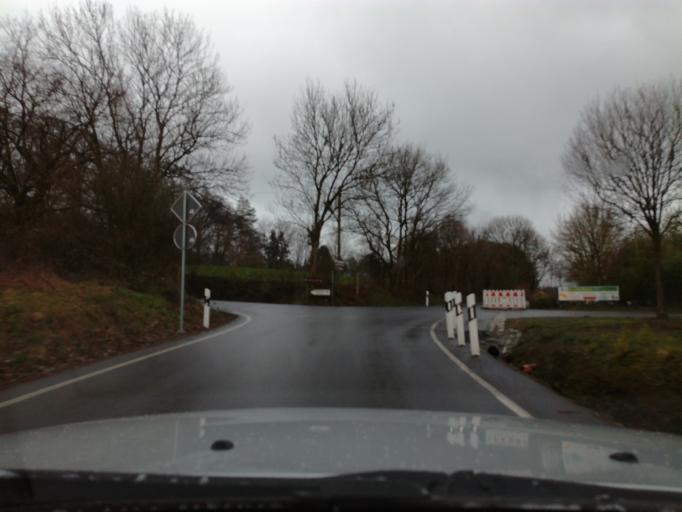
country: DE
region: North Rhine-Westphalia
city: Hattingen
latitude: 51.3595
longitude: 7.1921
